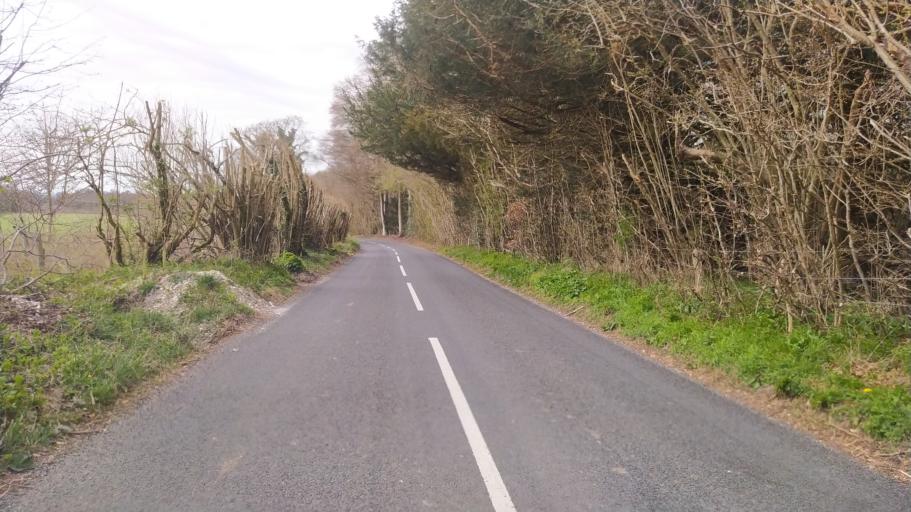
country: GB
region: England
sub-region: Hampshire
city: Bishops Waltham
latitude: 51.0120
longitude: -1.1920
